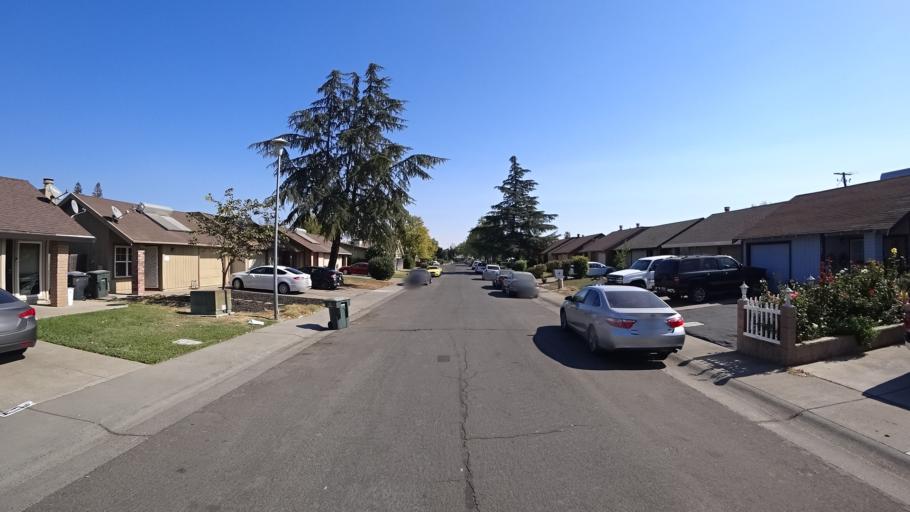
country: US
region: California
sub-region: Sacramento County
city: Parkway
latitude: 38.4935
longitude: -121.4778
